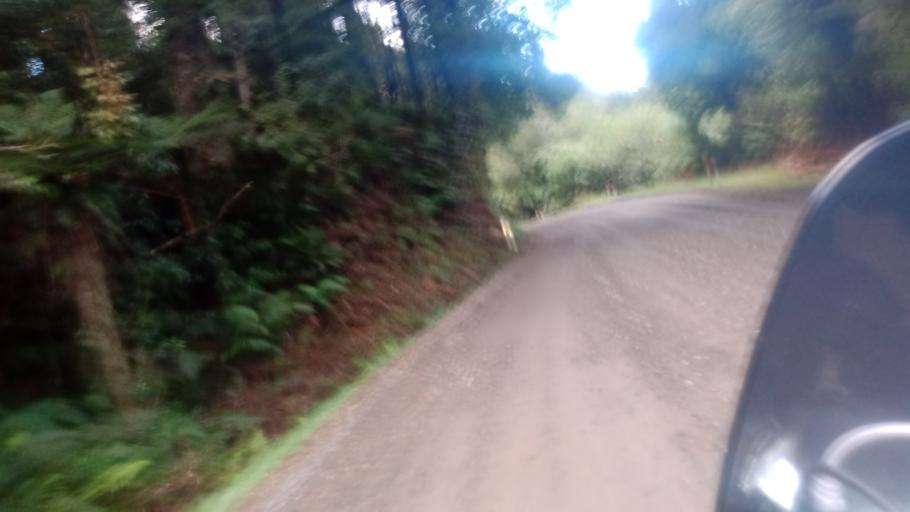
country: NZ
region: Hawke's Bay
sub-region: Wairoa District
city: Wairoa
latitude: -38.7396
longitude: 177.0984
